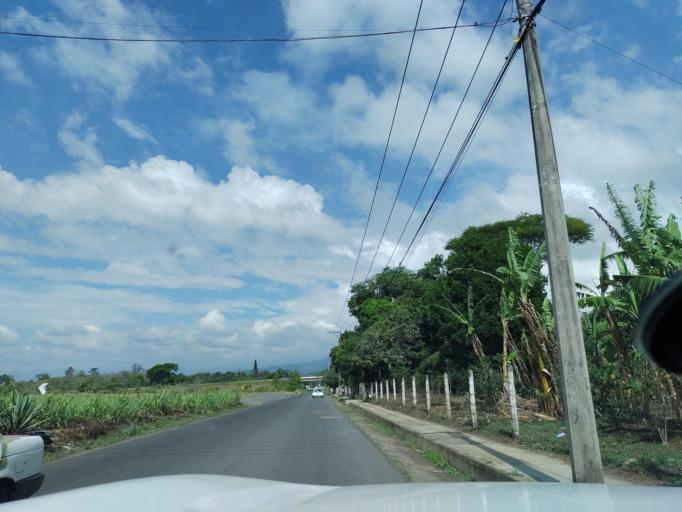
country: MX
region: Veracruz
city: Coatepec
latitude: 19.4811
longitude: -96.9376
